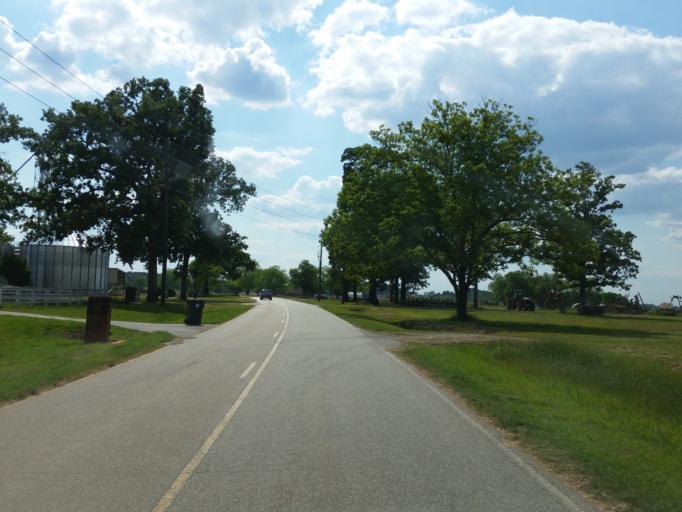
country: US
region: Georgia
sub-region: Houston County
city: Centerville
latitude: 32.5784
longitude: -83.7277
